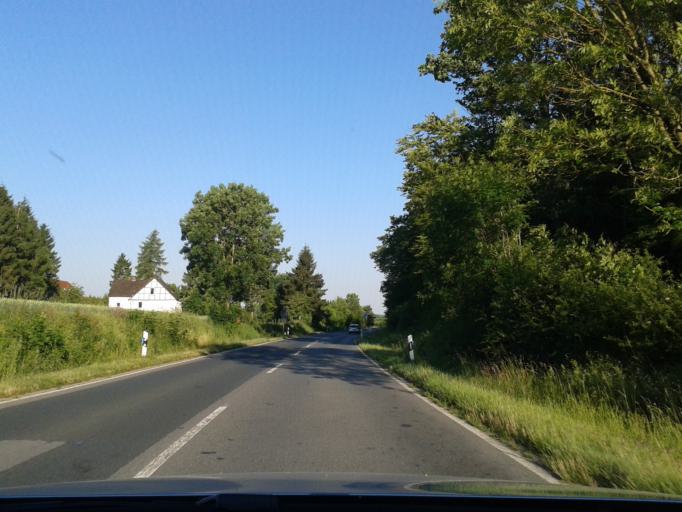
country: DE
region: North Rhine-Westphalia
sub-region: Regierungsbezirk Detmold
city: Barntrup
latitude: 51.9766
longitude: 9.1600
